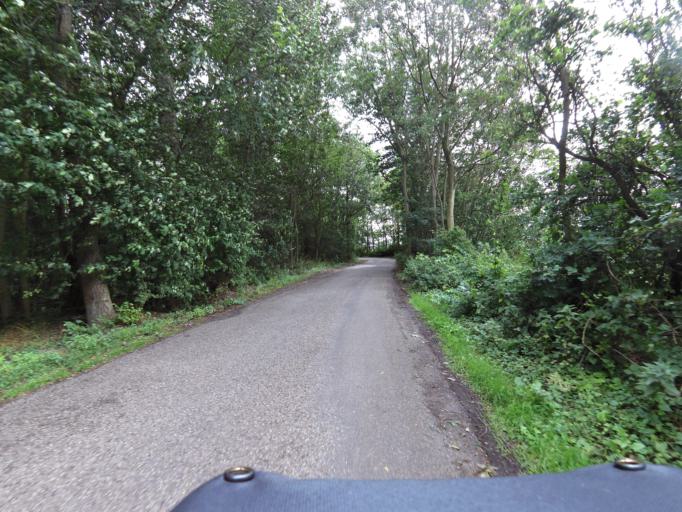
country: NL
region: South Holland
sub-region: Gemeente Goeree-Overflakkee
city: Goedereede
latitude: 51.8351
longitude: 3.9845
